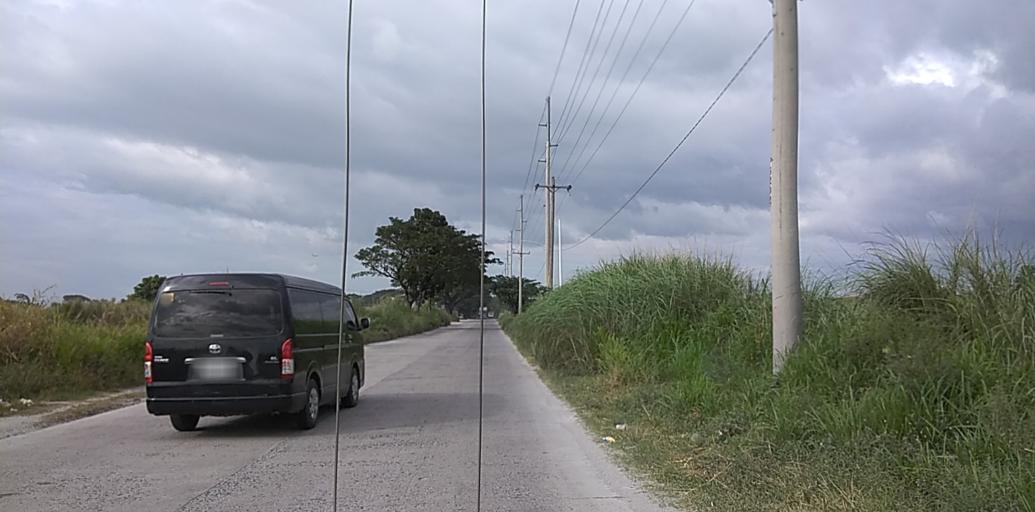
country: PH
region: Central Luzon
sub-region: Province of Pampanga
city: Porac
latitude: 15.0735
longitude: 120.5498
